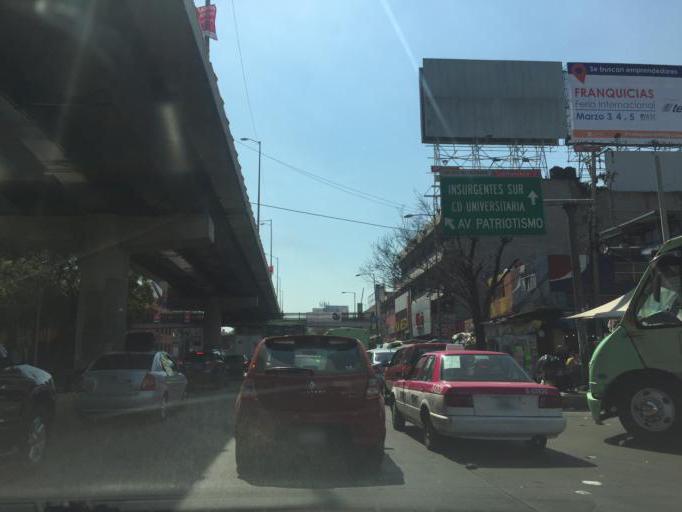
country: MX
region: Mexico City
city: Alvaro Obregon
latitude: 19.3750
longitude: -99.1878
